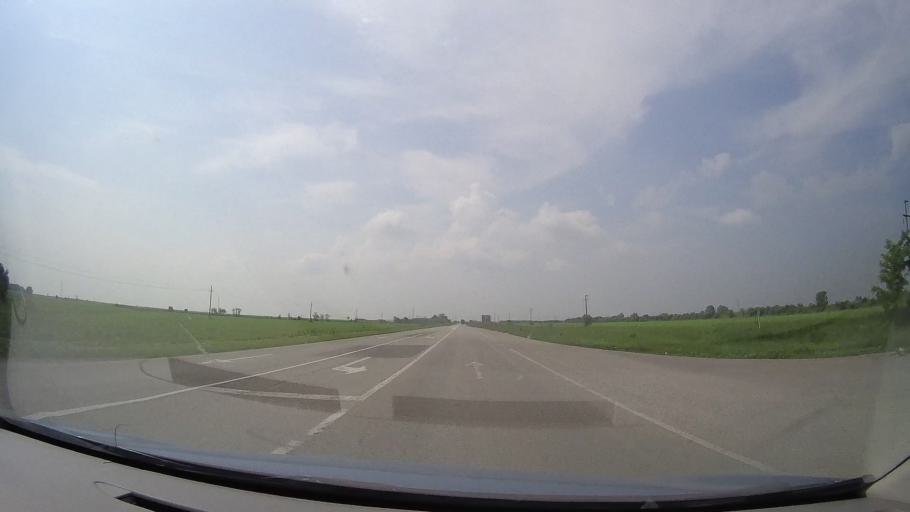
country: RS
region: Autonomna Pokrajina Vojvodina
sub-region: Juznobanatski Okrug
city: Kovacica
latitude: 45.0769
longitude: 20.6410
